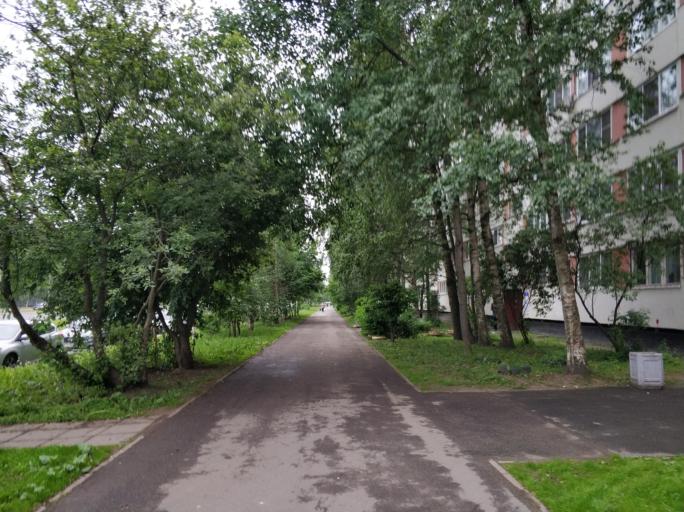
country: RU
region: St.-Petersburg
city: Grazhdanka
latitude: 60.0443
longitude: 30.4201
